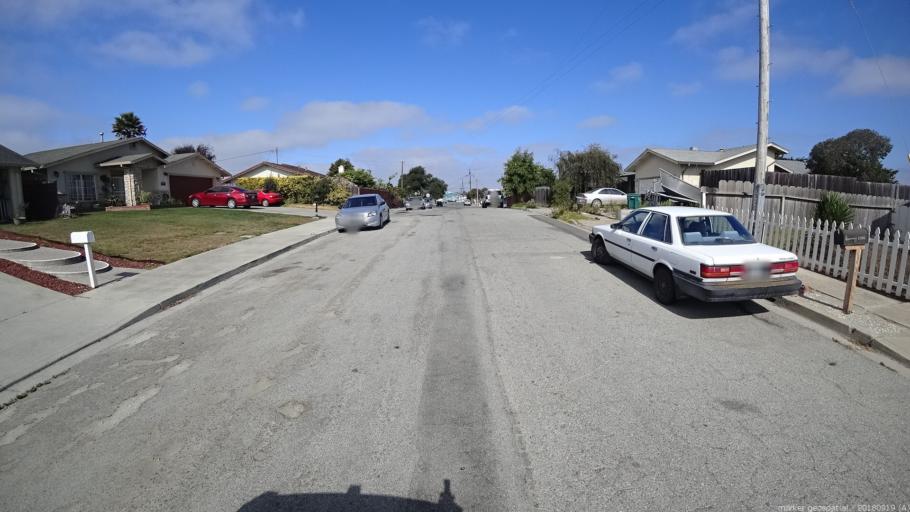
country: US
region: California
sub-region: Monterey County
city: Castroville
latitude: 36.7678
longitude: -121.7502
